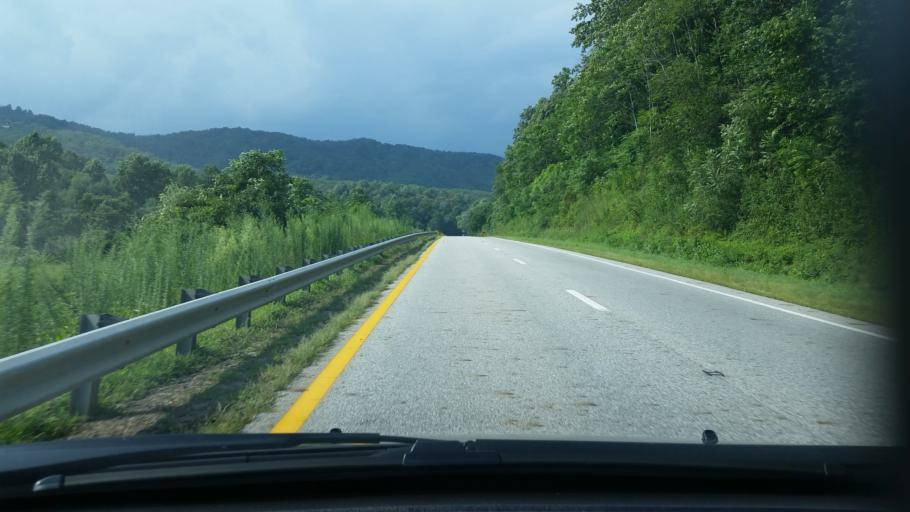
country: US
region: Virginia
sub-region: Nelson County
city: Lovingston
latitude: 37.7989
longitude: -78.8619
